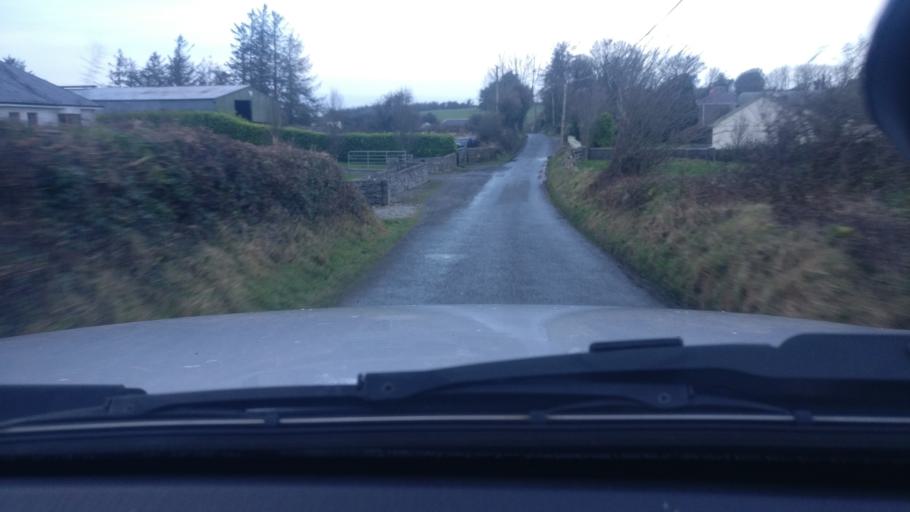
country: IE
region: Connaught
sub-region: County Galway
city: Loughrea
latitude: 53.1696
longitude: -8.5838
